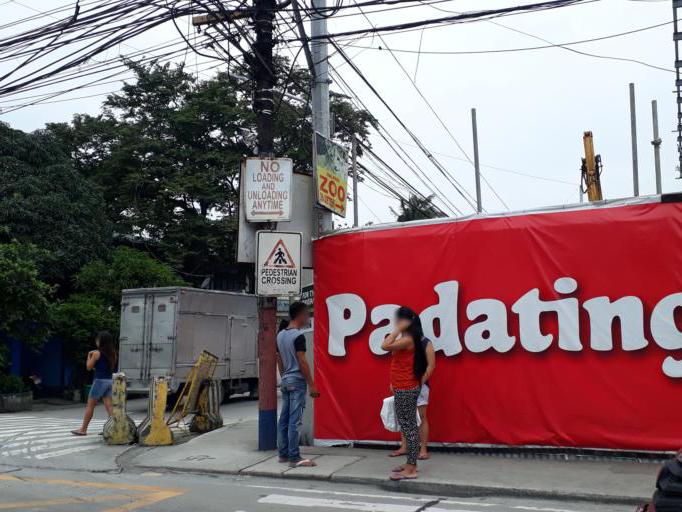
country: PH
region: Metro Manila
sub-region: Caloocan City
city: Niugan
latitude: 14.6637
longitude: 120.9842
